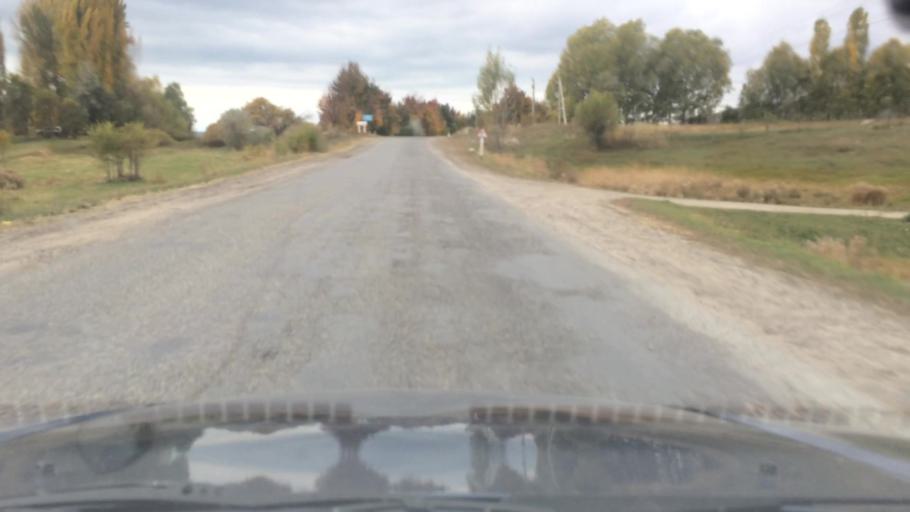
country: KG
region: Ysyk-Koel
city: Tyup
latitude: 42.7666
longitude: 78.1821
